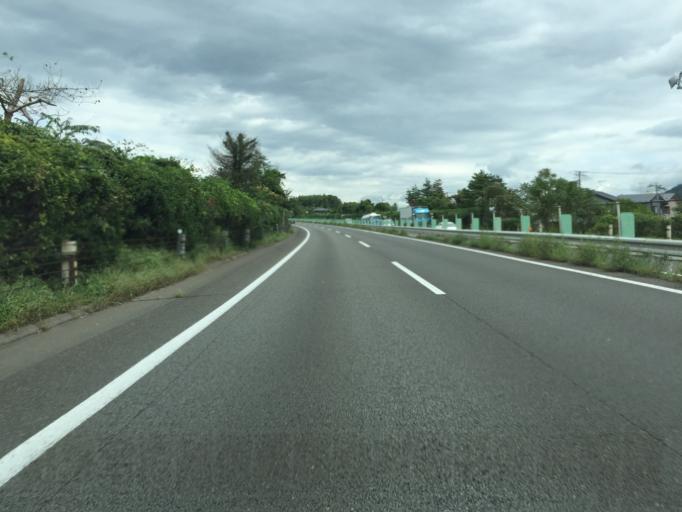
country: JP
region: Miyagi
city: Shiroishi
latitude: 38.0514
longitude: 140.6521
